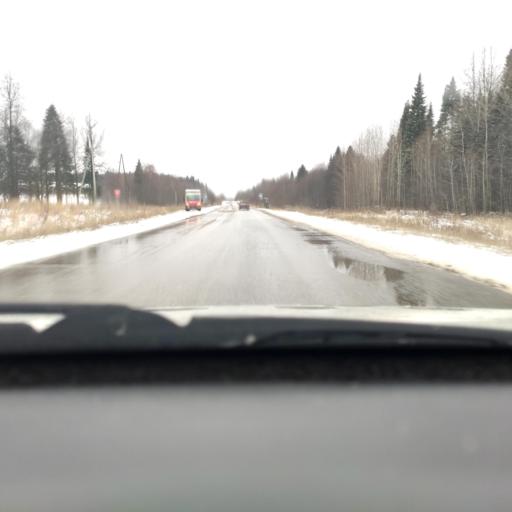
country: RU
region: Perm
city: Ferma
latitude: 57.9910
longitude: 56.3754
